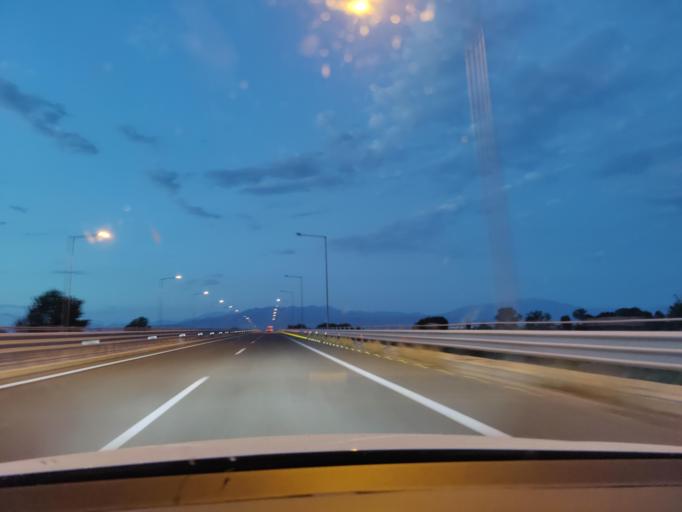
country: GR
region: Central Macedonia
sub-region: Nomos Serron
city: Strymoniko
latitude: 41.0542
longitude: 23.3409
